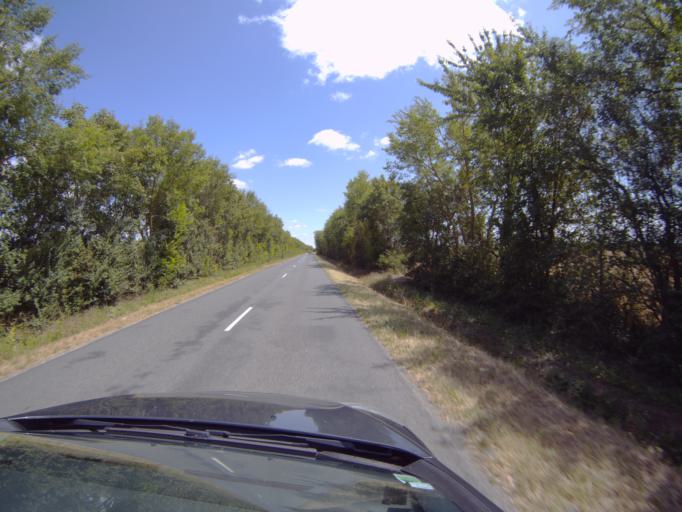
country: FR
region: Poitou-Charentes
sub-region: Departement de la Charente-Maritime
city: Saint-Jean-de-Liversay
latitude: 46.2569
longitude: -0.8477
